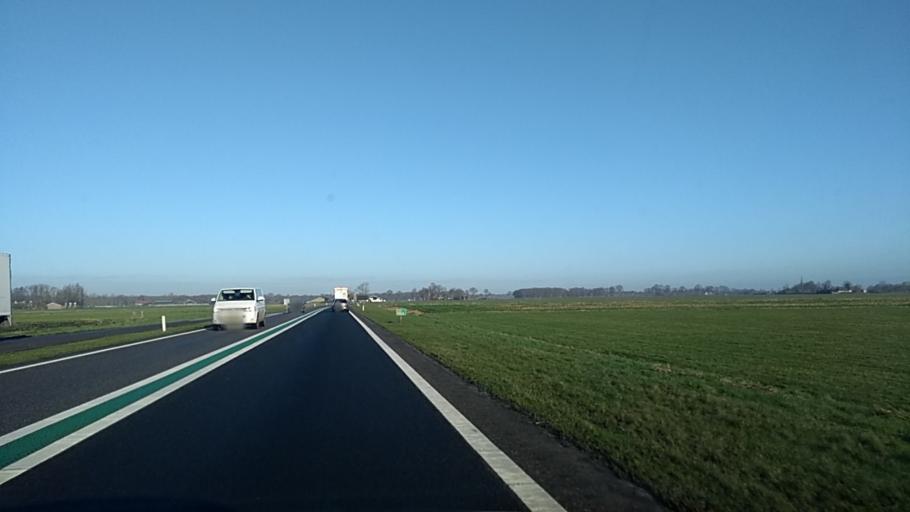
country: NL
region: Overijssel
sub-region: Gemeente Twenterand
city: Den Ham
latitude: 52.5799
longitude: 6.4148
